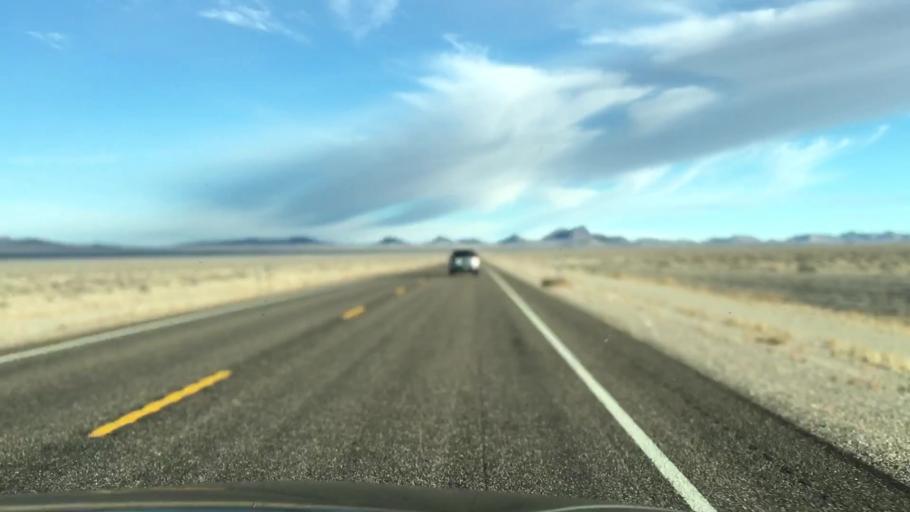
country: US
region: Nevada
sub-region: Nye County
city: Tonopah
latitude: 38.1247
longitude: -117.4060
